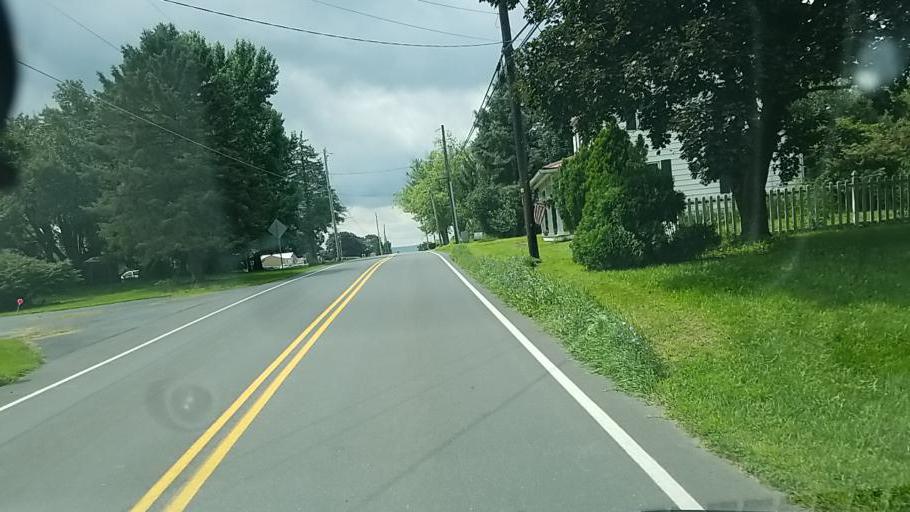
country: US
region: Pennsylvania
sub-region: Dauphin County
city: Elizabethville
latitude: 40.5065
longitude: -76.8800
